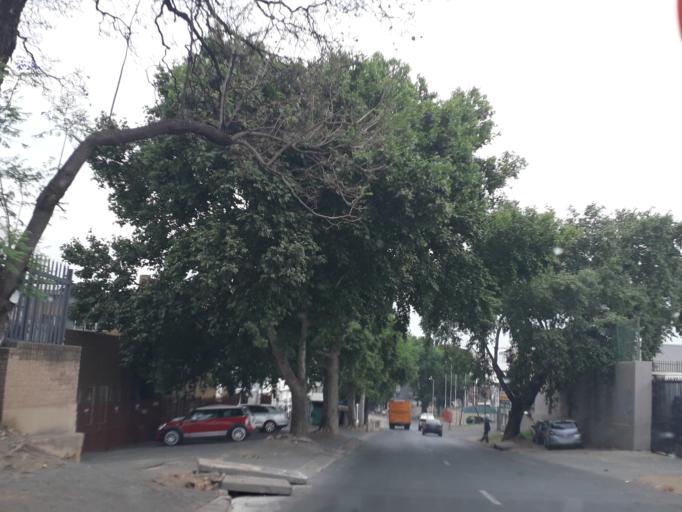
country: ZA
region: Gauteng
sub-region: City of Johannesburg Metropolitan Municipality
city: Modderfontein
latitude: -26.1084
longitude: 28.0832
